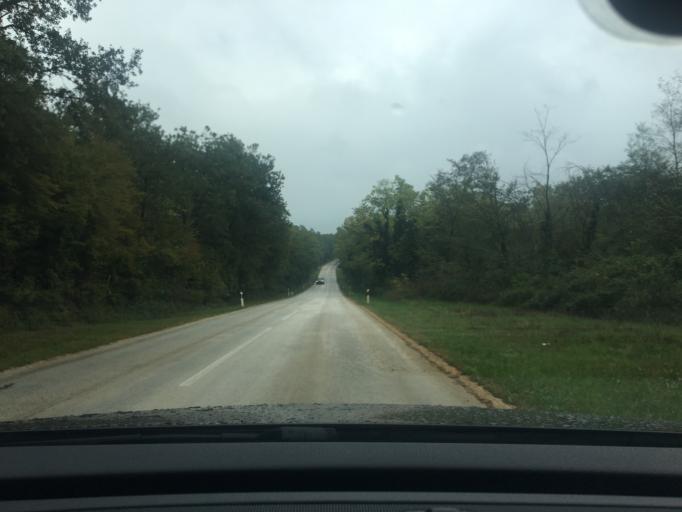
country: HR
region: Istarska
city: Novigrad
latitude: 45.3538
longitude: 13.6004
